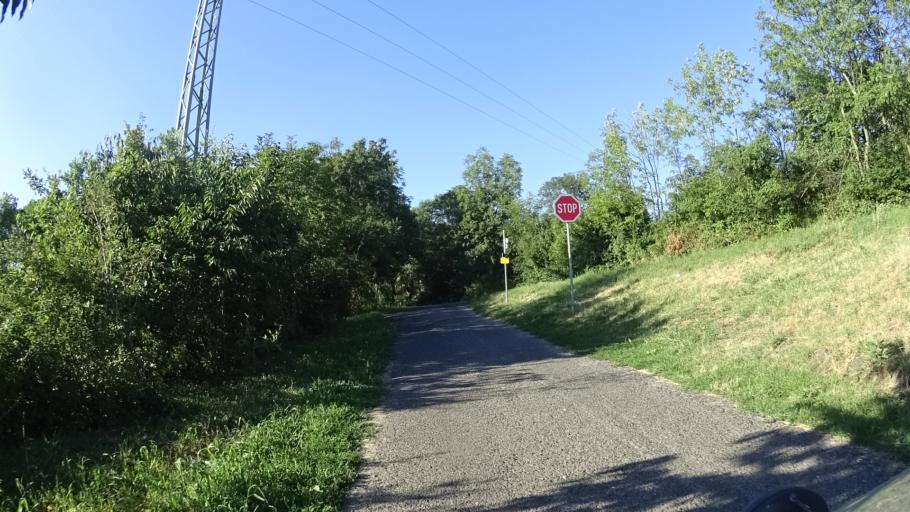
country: CZ
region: Ustecky
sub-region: Okres Litomerice
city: Litomerice
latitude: 50.5701
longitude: 14.1071
